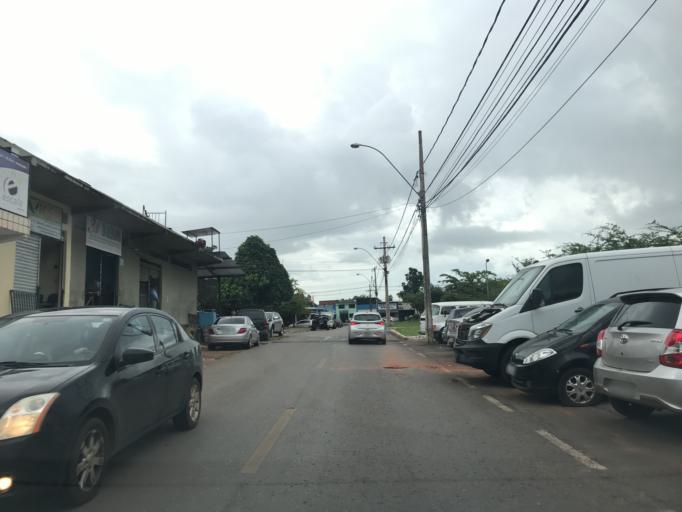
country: BR
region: Federal District
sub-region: Brasilia
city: Brasilia
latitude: -15.7880
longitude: -47.9181
